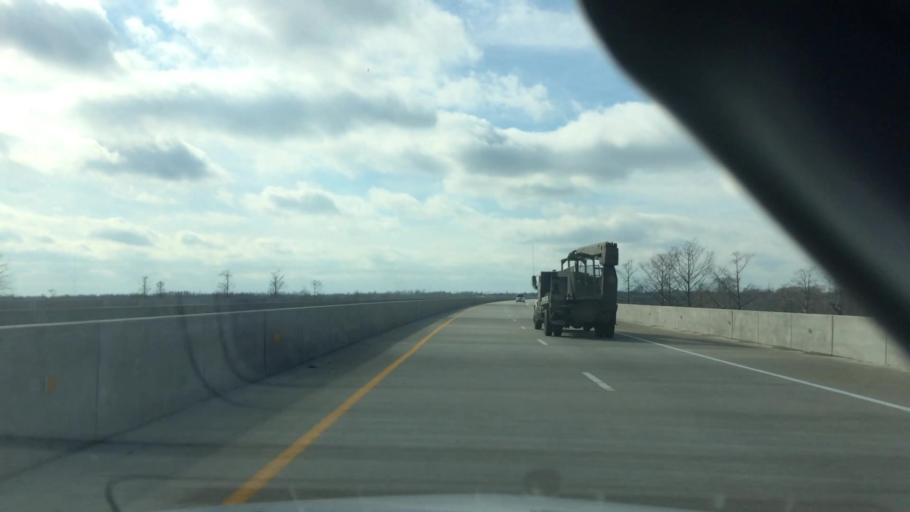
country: US
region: North Carolina
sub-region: Brunswick County
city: Navassa
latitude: 34.2756
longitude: -77.9856
